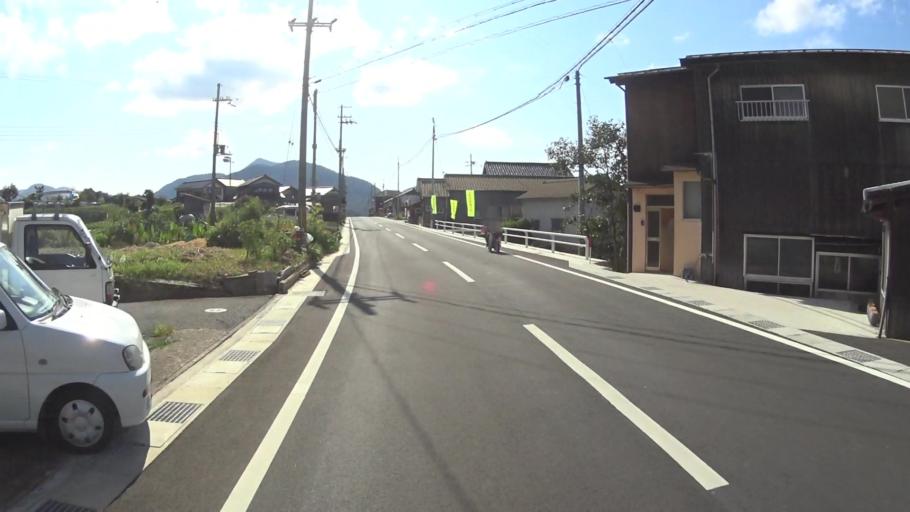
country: JP
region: Kyoto
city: Miyazu
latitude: 35.7589
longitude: 135.1797
